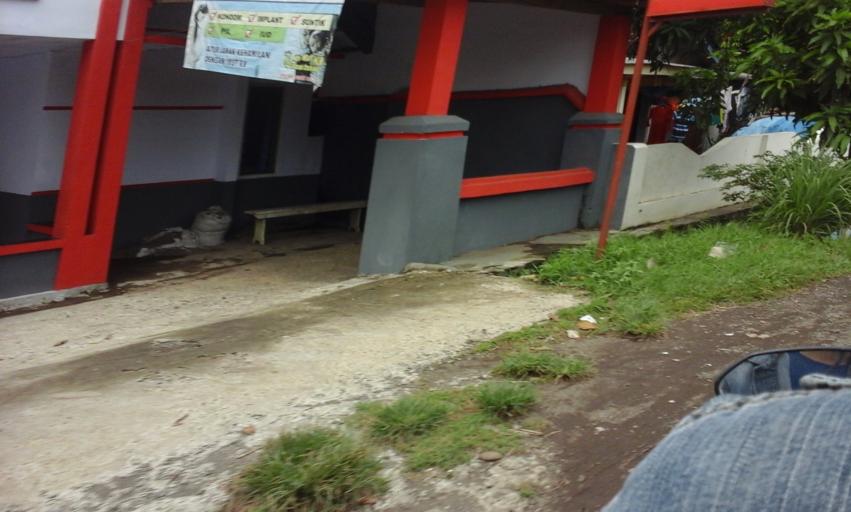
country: ID
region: East Java
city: Gambirono
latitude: -8.1938
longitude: 113.5046
